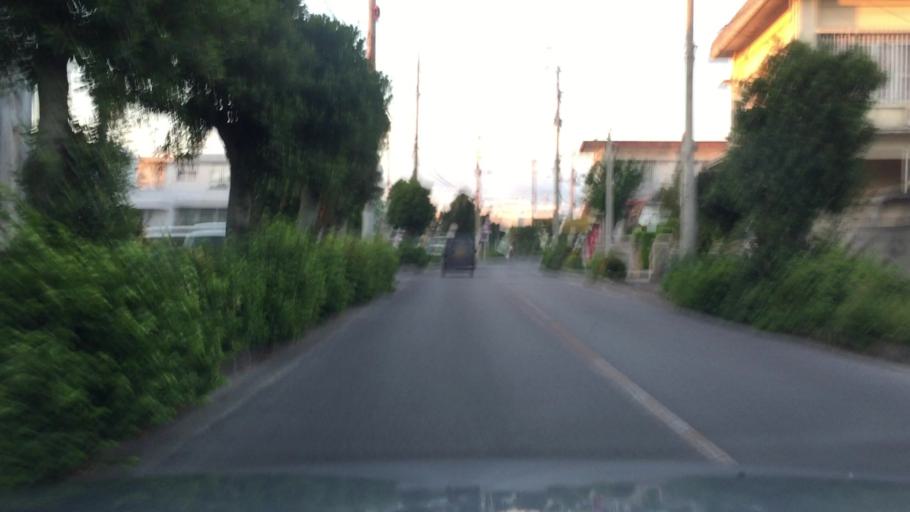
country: JP
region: Okinawa
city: Ishigaki
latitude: 24.3476
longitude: 124.1625
